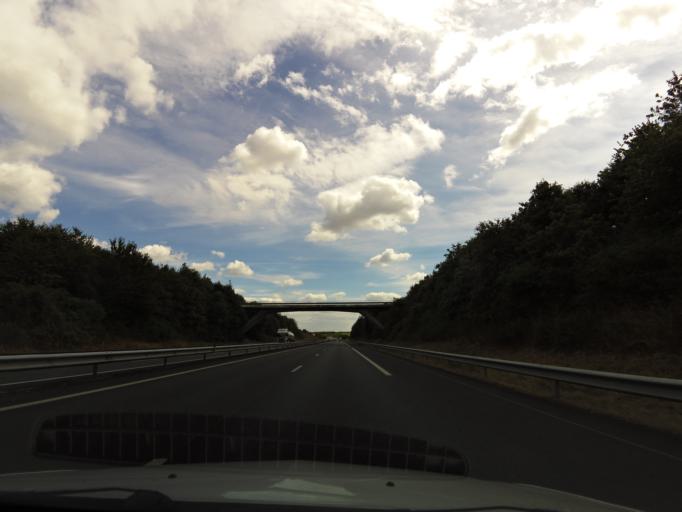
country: FR
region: Pays de la Loire
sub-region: Departement de la Vendee
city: Les Brouzils
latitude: 46.9191
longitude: -1.3289
